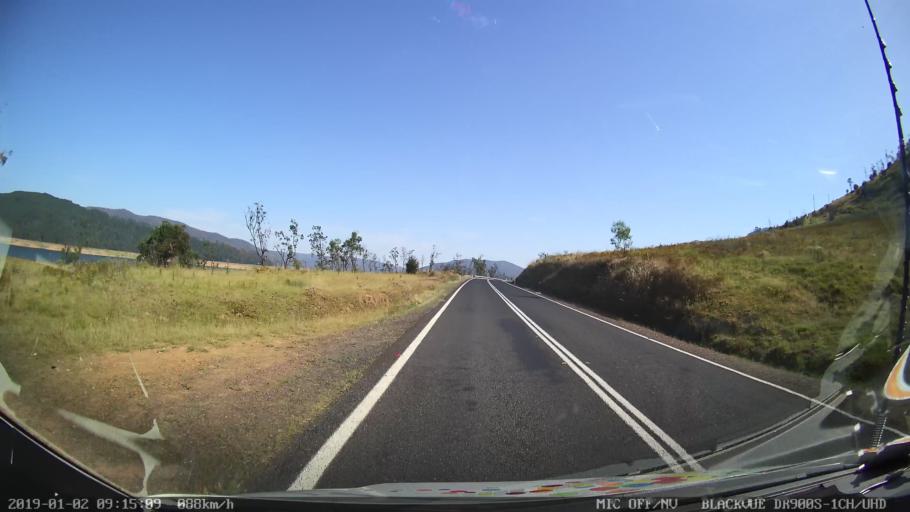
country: AU
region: New South Wales
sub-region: Tumut Shire
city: Tumut
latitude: -35.4686
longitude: 148.2786
